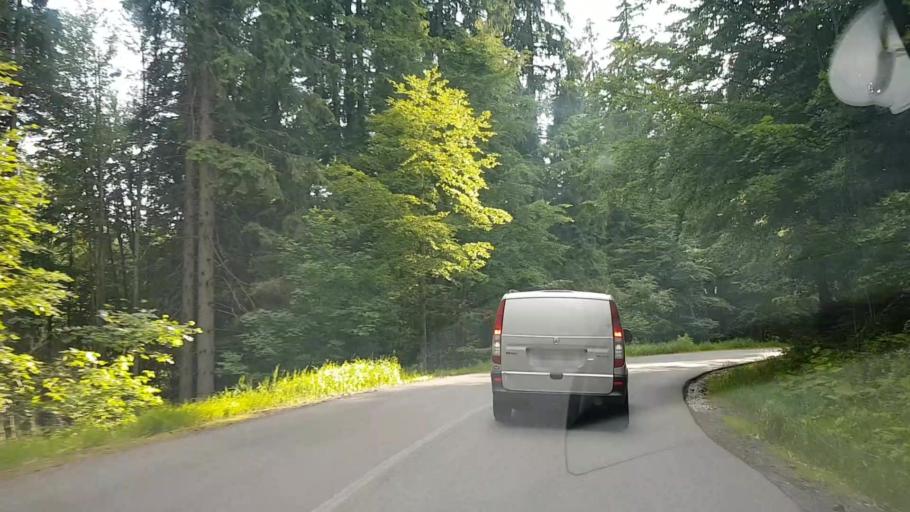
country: RO
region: Harghita
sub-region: Comuna Varsag
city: Varsag
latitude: 46.6678
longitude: 25.3238
